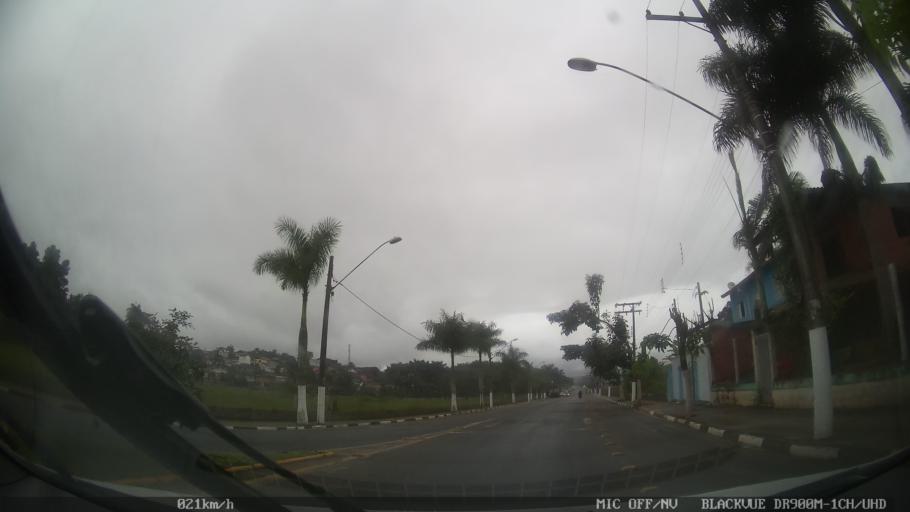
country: BR
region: Sao Paulo
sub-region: Juquia
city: Juquia
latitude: -24.3191
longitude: -47.6404
